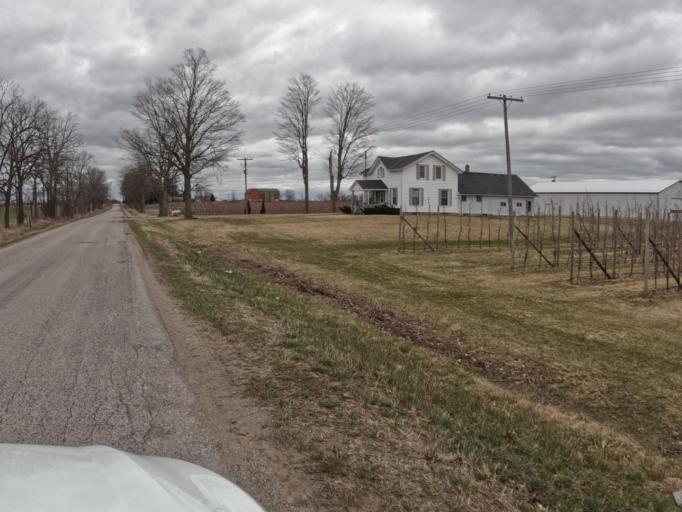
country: CA
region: Ontario
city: Norfolk County
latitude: 42.9434
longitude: -80.4024
